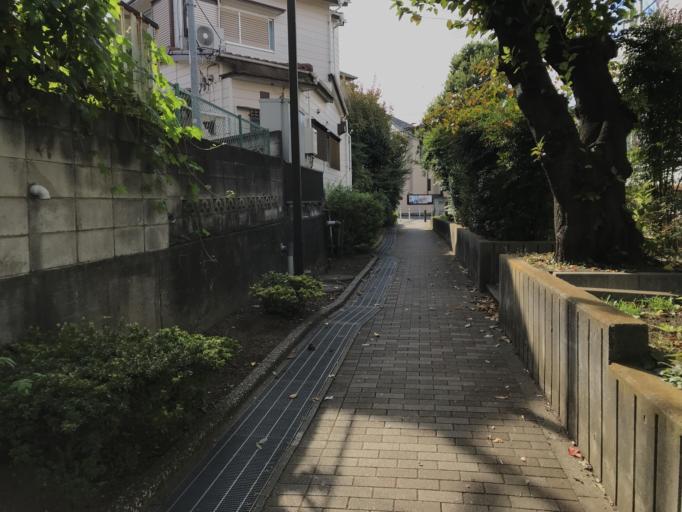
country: JP
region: Tokyo
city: Musashino
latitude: 35.7431
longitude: 139.5761
